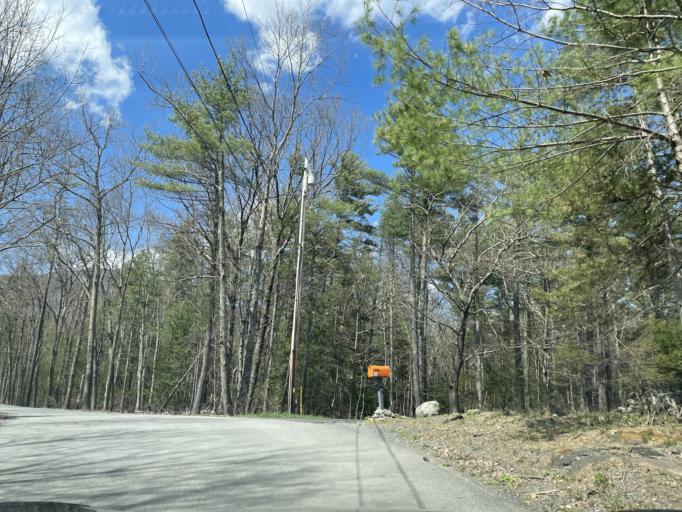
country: US
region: New York
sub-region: Ulster County
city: Zena
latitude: 42.0612
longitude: -74.0630
